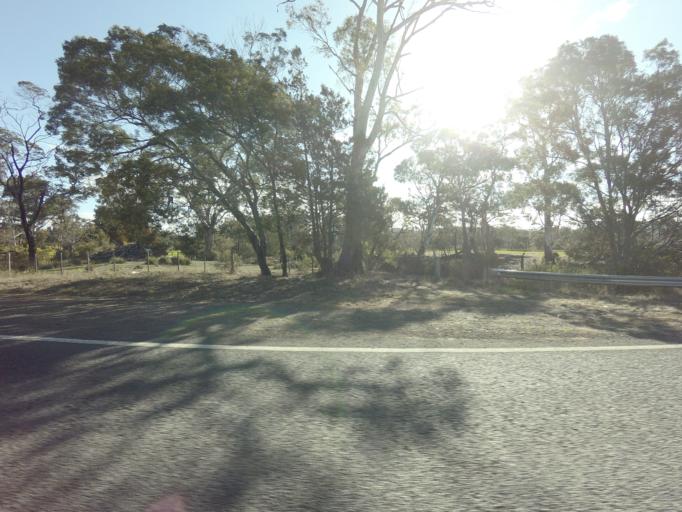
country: AU
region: Tasmania
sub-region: Sorell
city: Sorell
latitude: -42.5241
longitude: 147.8982
